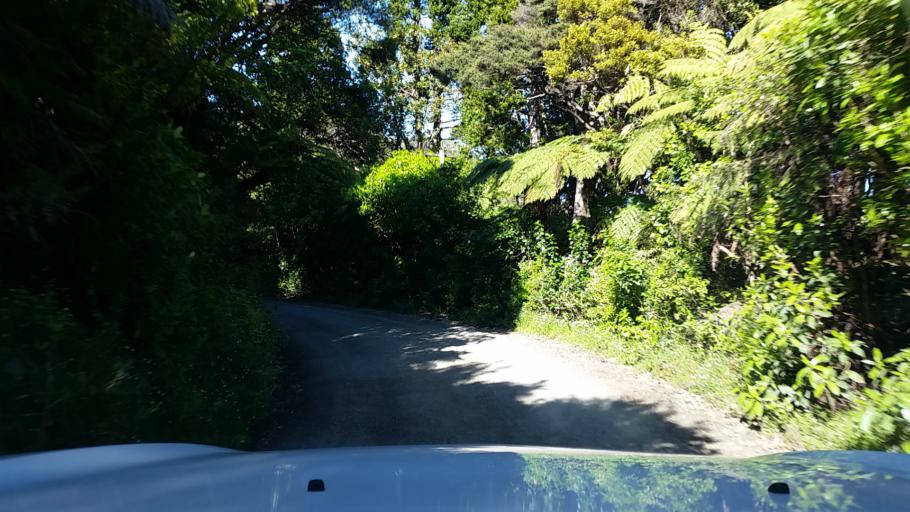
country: NZ
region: Auckland
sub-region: Auckland
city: Titirangi
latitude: -37.0292
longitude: 174.5256
